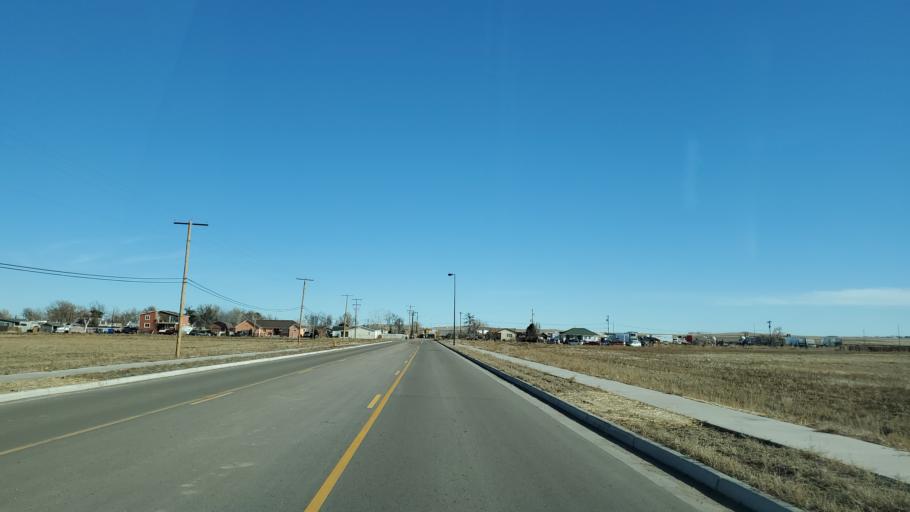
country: US
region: Colorado
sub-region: Adams County
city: Derby
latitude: 39.8490
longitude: -104.8963
